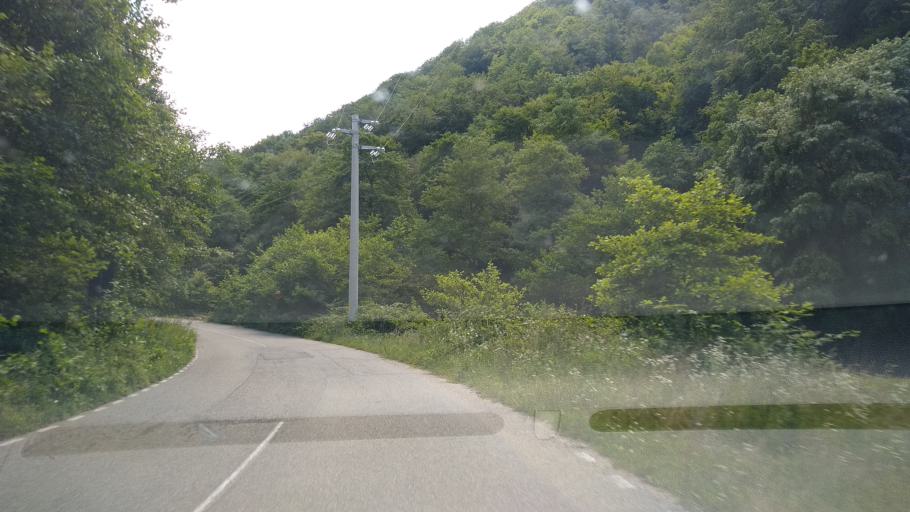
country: RO
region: Hunedoara
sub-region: Comuna Orastioara de Sus
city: Orastioara de Sus
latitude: 45.6673
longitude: 23.1706
